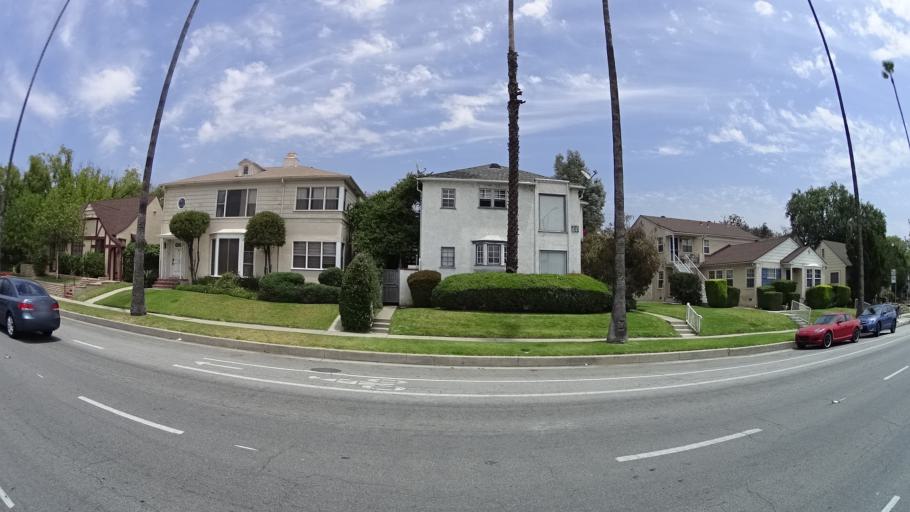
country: US
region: California
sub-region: Los Angeles County
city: North Glendale
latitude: 34.1631
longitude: -118.2787
